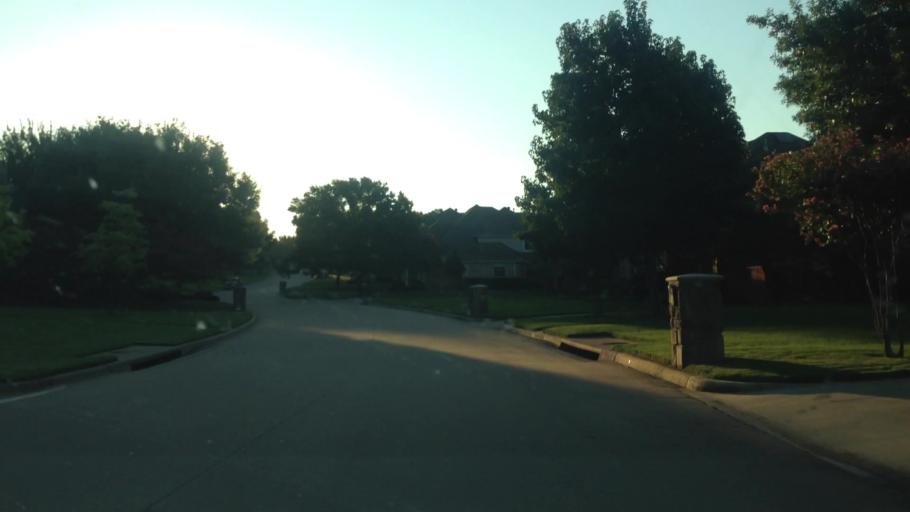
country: US
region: Texas
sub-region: Tarrant County
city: Southlake
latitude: 32.9354
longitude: -97.1289
